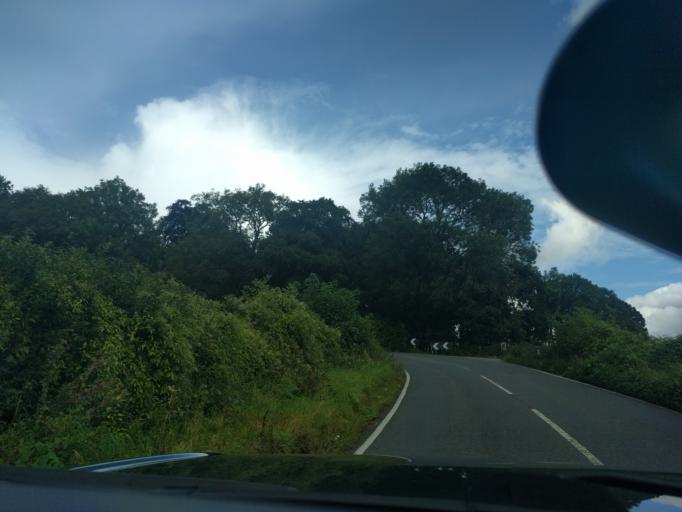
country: GB
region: England
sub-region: Bath and North East Somerset
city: Freshford
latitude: 51.3612
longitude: -2.3178
